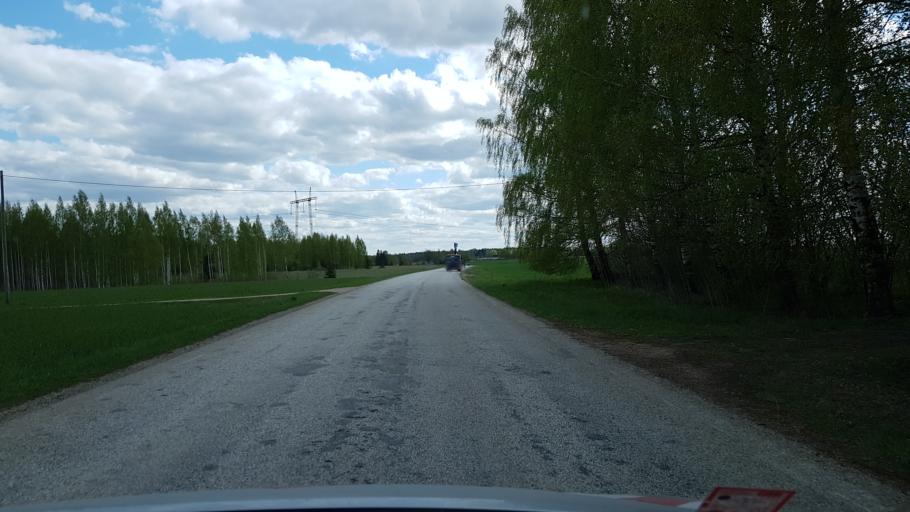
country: EE
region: Tartu
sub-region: UElenurme vald
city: Ulenurme
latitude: 58.2777
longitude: 26.9062
